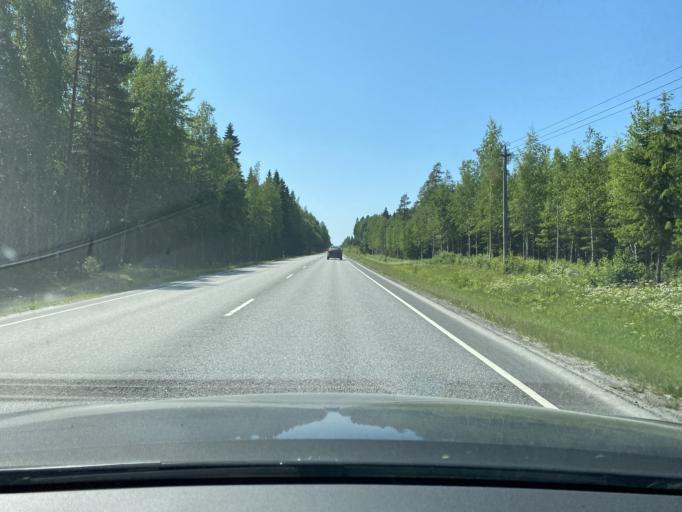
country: FI
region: Pirkanmaa
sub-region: Tampere
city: Nokia
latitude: 61.4313
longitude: 23.4000
